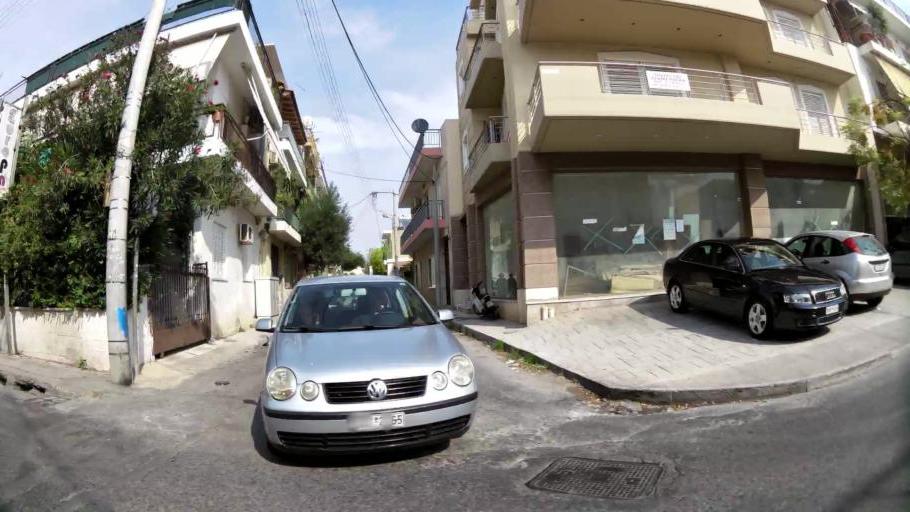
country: GR
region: Attica
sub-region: Nomarchia Athinas
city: Peristeri
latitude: 38.0187
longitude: 23.6836
